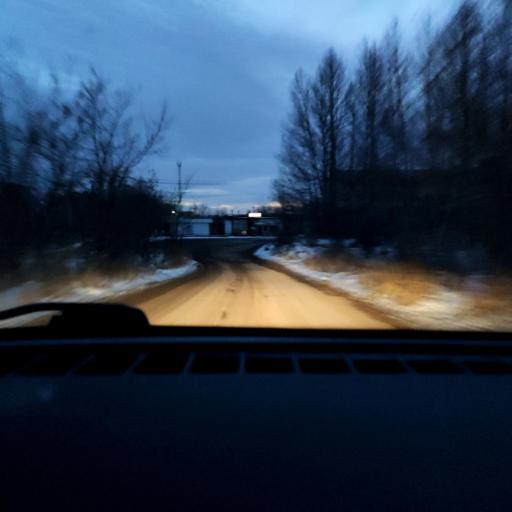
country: RU
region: Perm
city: Kondratovo
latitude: 57.9577
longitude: 56.1523
